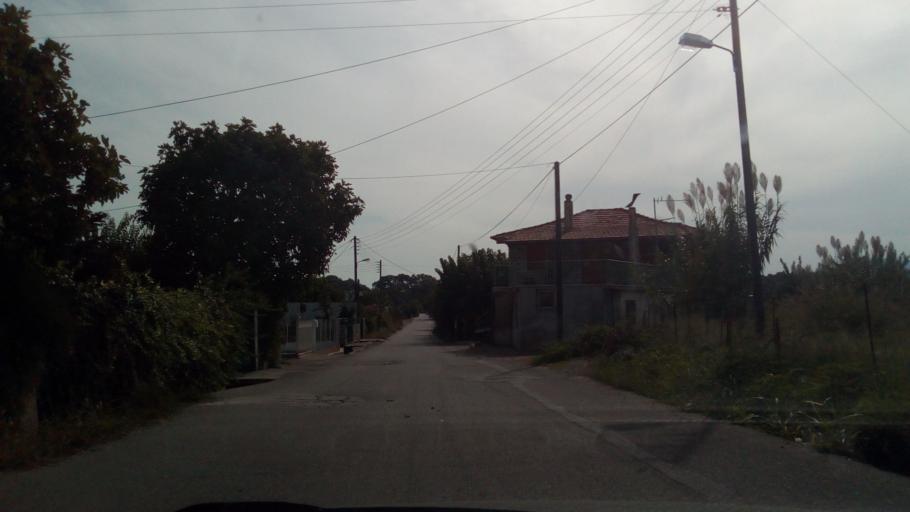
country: GR
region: West Greece
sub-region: Nomos Aitolias kai Akarnanias
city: Nafpaktos
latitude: 38.4013
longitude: 21.8625
